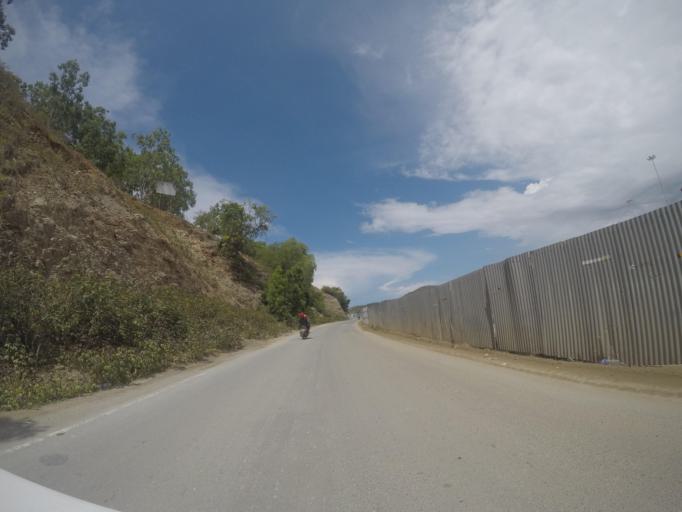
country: TL
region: Dili
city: Dili
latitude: -8.5697
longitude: 125.4713
